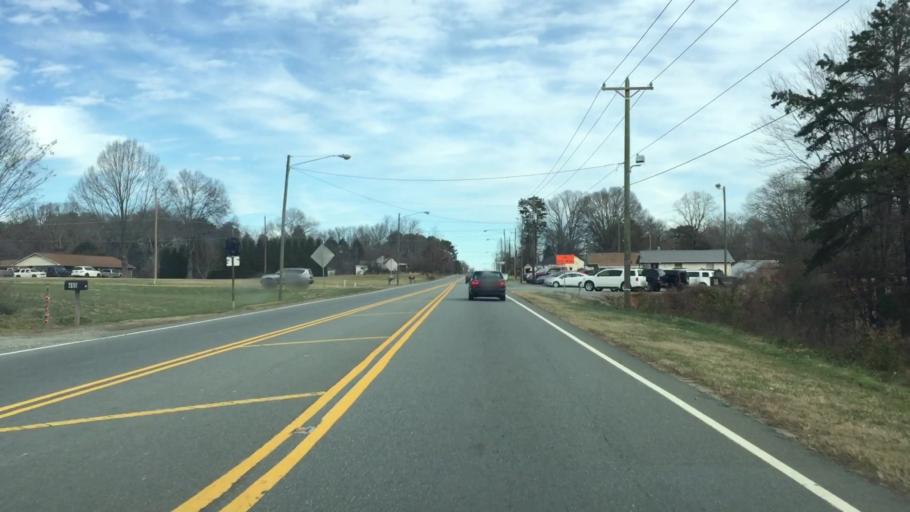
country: US
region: North Carolina
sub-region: Forsyth County
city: Walkertown
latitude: 36.1530
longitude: -80.1495
